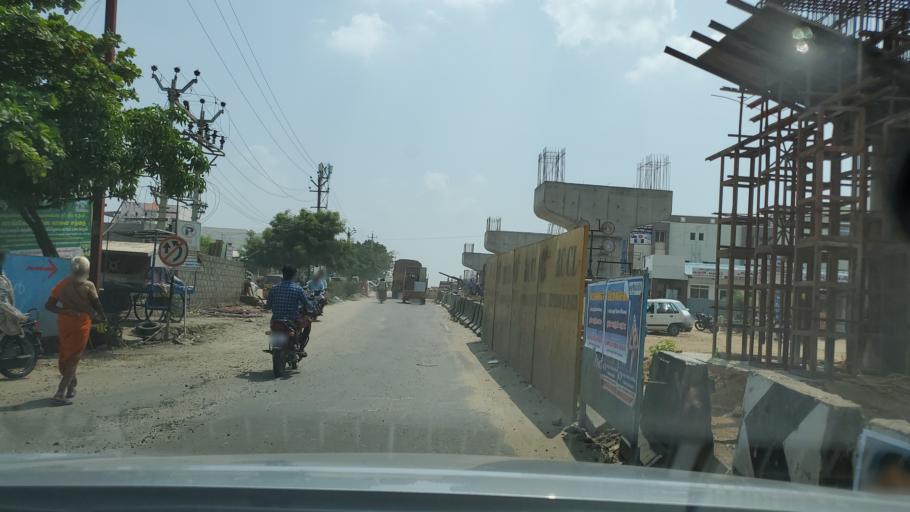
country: IN
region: Tamil Nadu
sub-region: Tiruppur
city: Dharapuram
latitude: 10.7328
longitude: 77.5185
